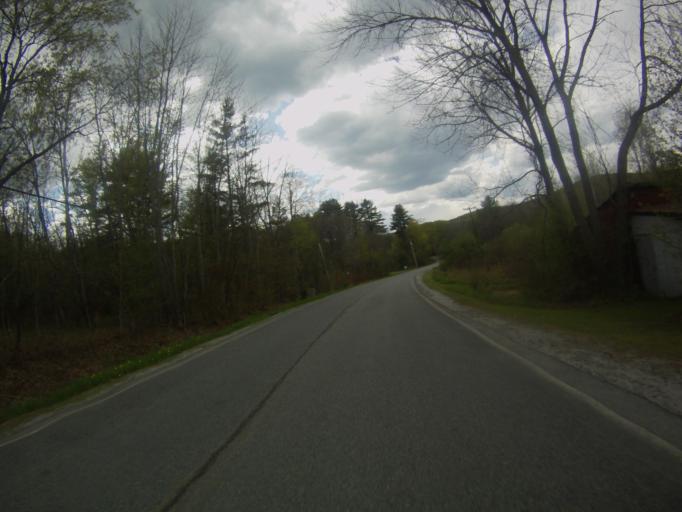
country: US
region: New York
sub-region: Essex County
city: Mineville
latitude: 44.0525
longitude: -73.5449
